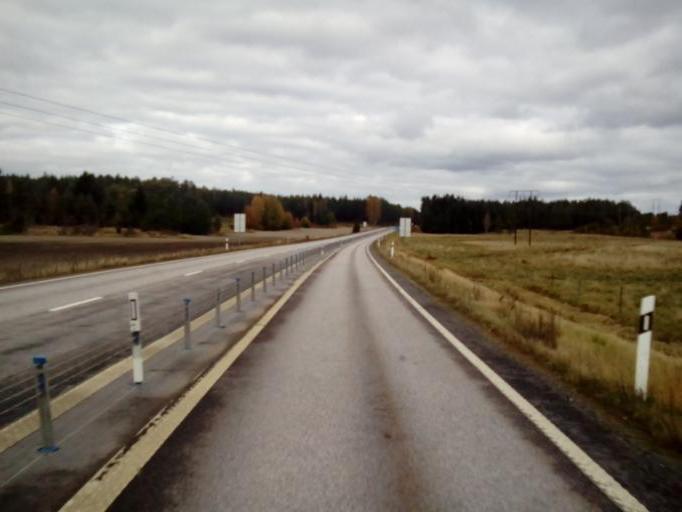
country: SE
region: OEstergoetland
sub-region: Valdemarsviks Kommun
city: Valdemarsvik
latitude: 58.1230
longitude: 16.5348
